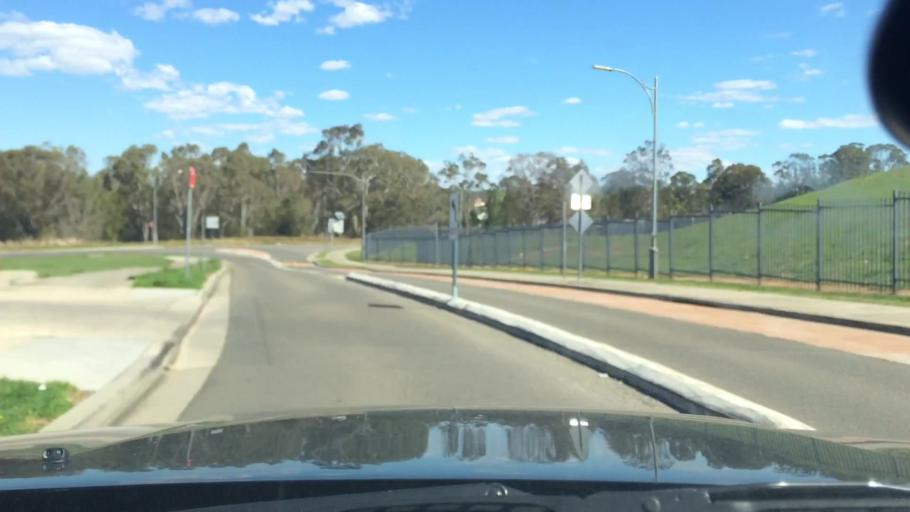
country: AU
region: New South Wales
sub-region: Campbelltown Municipality
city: Denham Court
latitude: -33.9393
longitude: 150.8439
